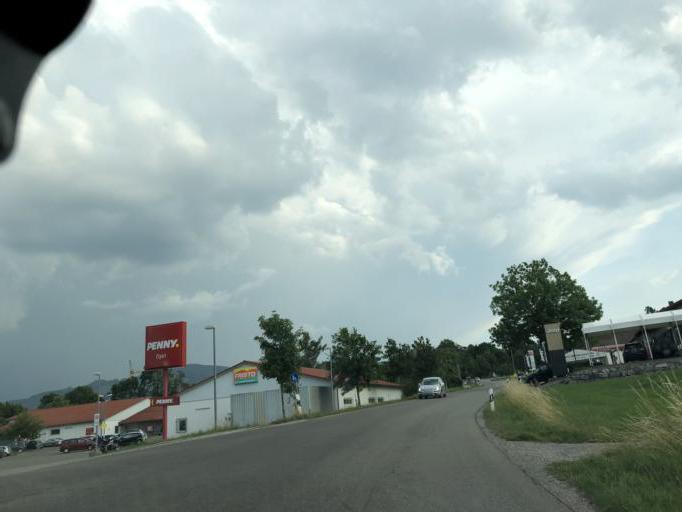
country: DE
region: Bavaria
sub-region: Swabia
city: Oy-Mittelberg
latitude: 47.6493
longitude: 10.4552
